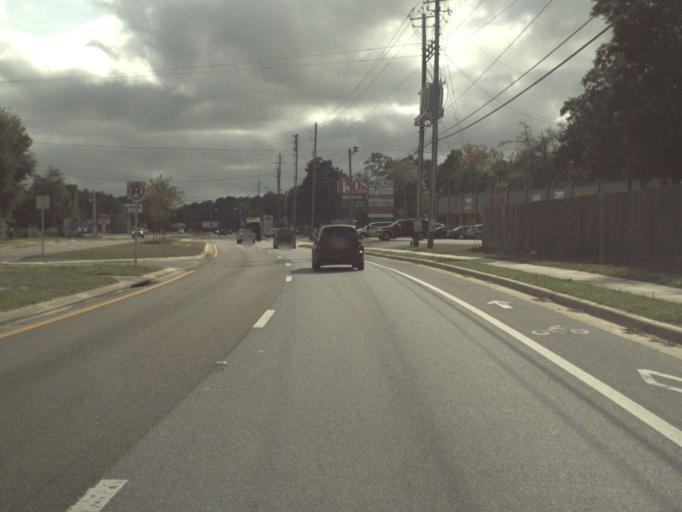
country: US
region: Florida
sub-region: Santa Rosa County
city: Milton
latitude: 30.6250
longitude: -87.0569
